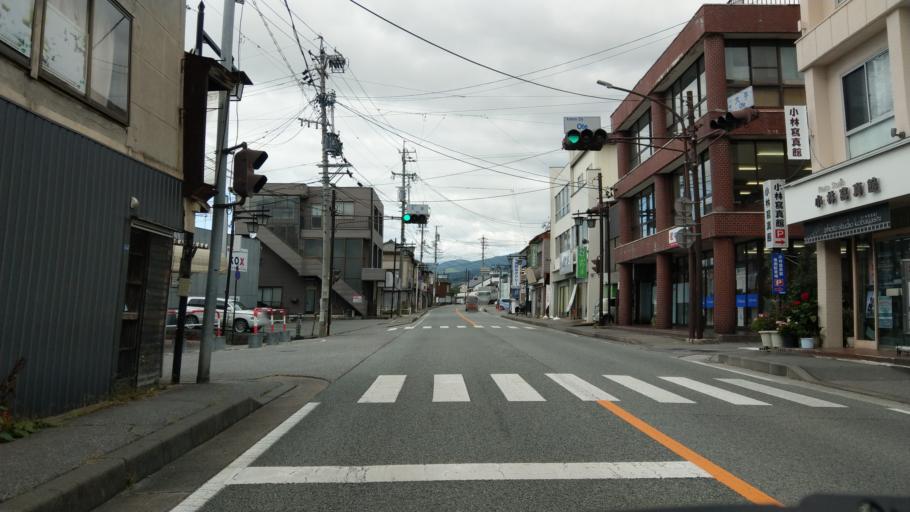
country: JP
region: Nagano
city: Komoro
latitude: 36.3280
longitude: 138.4229
